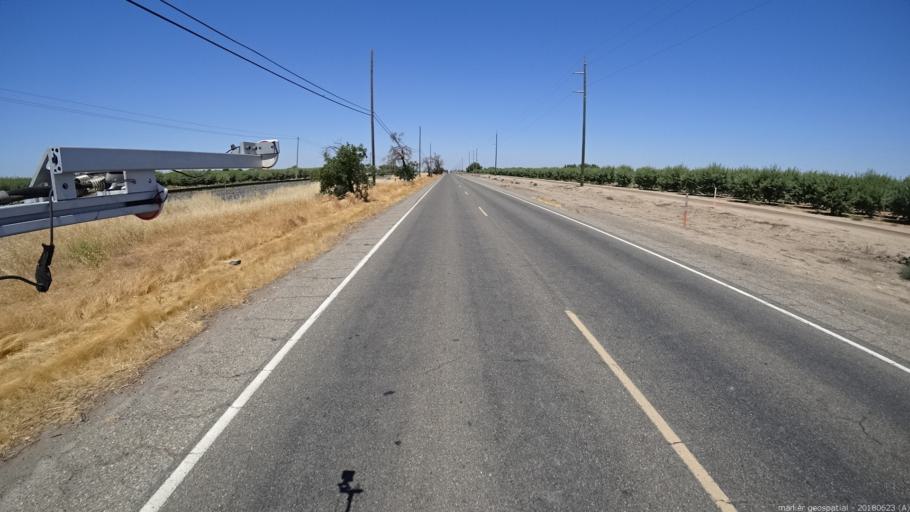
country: US
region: California
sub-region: Madera County
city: Chowchilla
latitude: 37.1036
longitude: -120.2309
